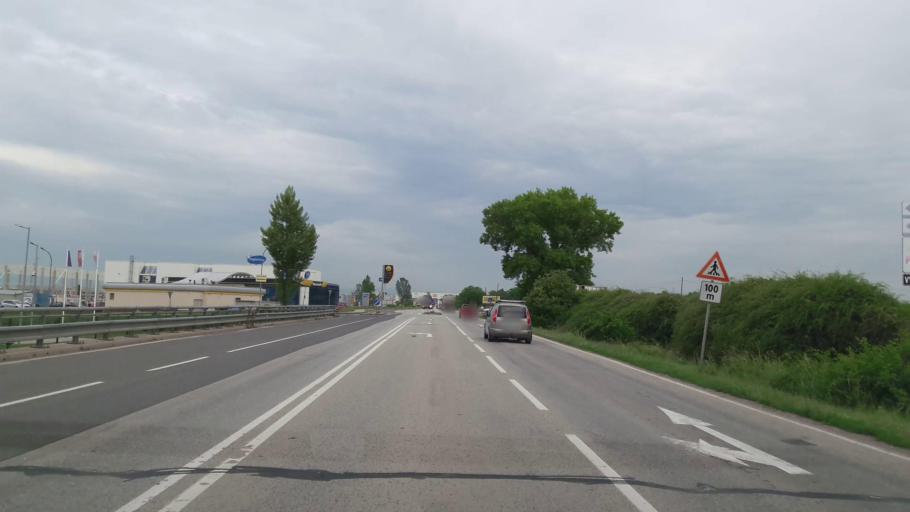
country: SK
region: Bratislavsky
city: Senec
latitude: 48.2304
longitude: 17.3752
